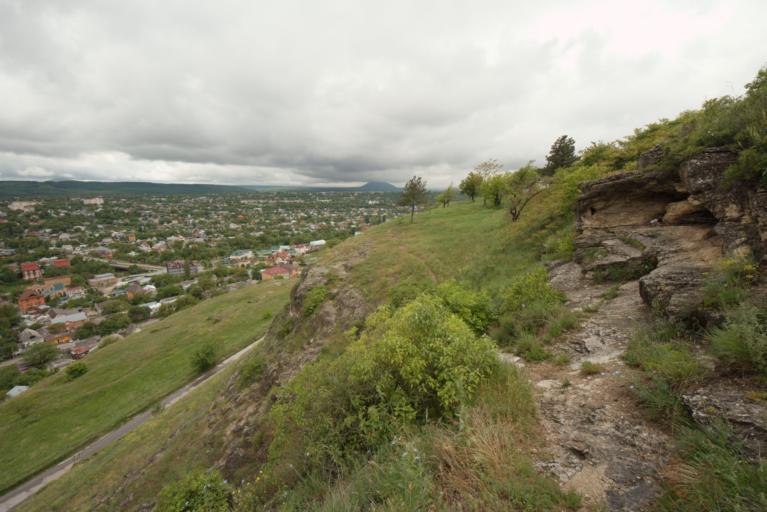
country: RU
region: Stavropol'skiy
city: Goryachevodskiy
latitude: 44.0370
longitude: 43.0869
